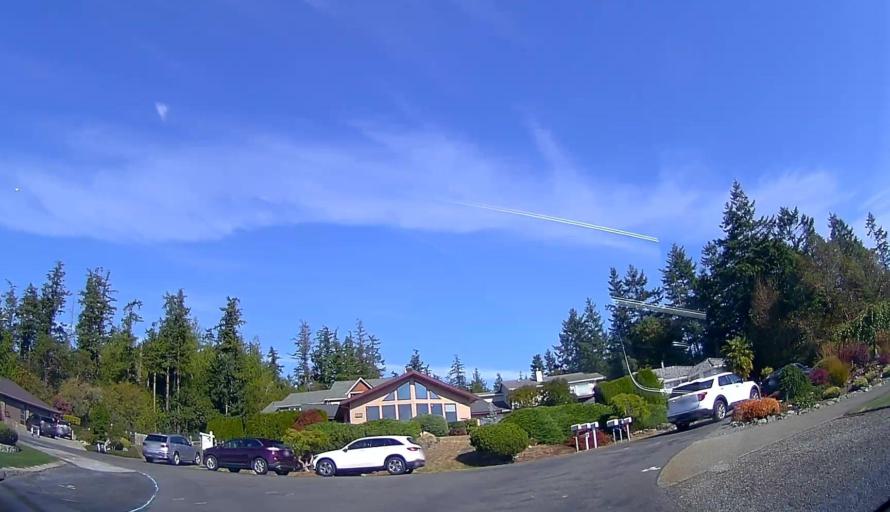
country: US
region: Washington
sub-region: Island County
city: Camano
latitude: 48.1841
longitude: -122.5333
